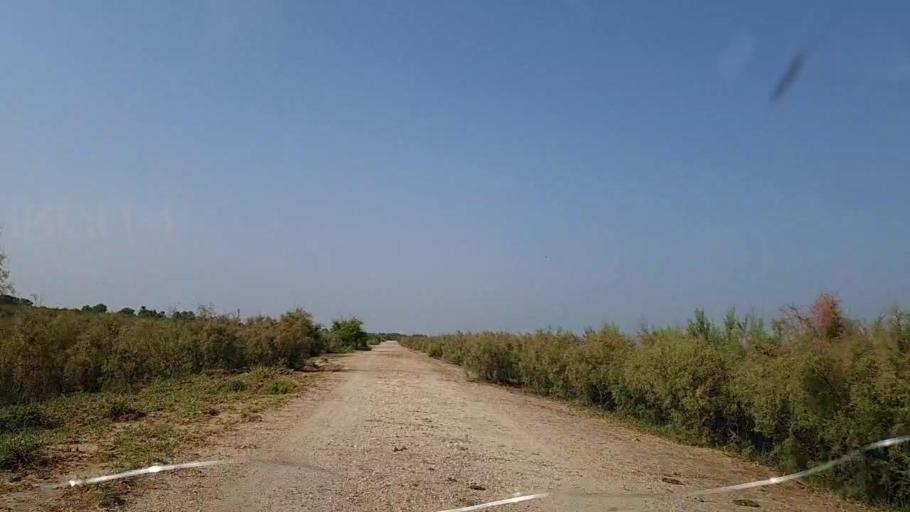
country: PK
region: Sindh
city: Khanpur
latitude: 27.7012
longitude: 69.3856
